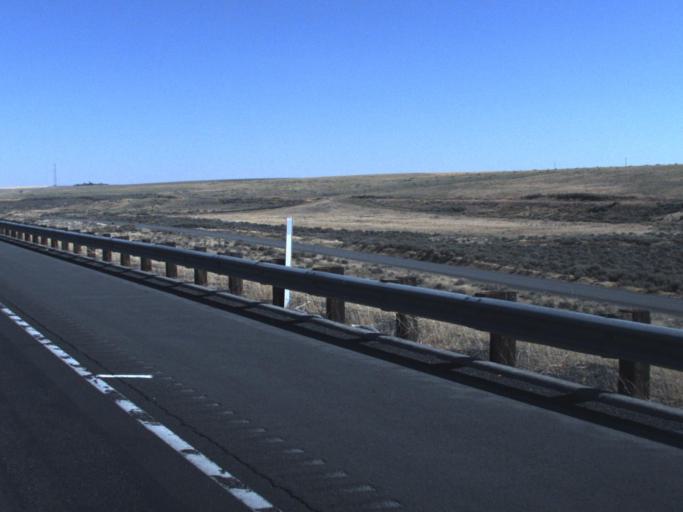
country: US
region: Washington
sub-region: Adams County
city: Ritzville
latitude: 47.0993
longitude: -118.6112
